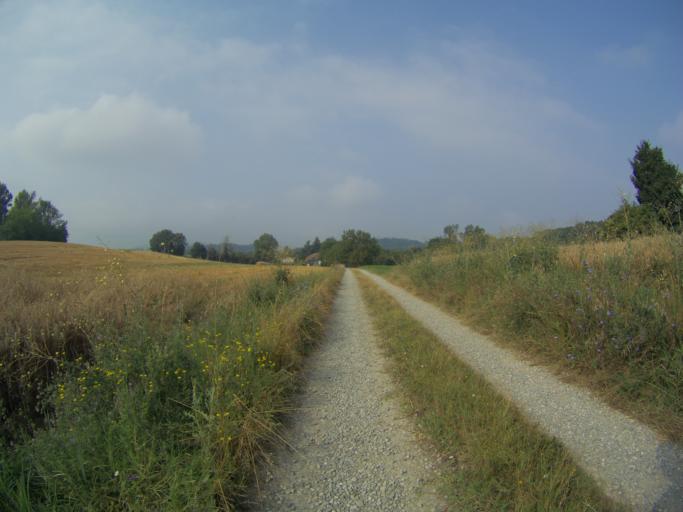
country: IT
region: Emilia-Romagna
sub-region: Provincia di Reggio Emilia
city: Albinea
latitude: 44.6200
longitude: 10.6233
